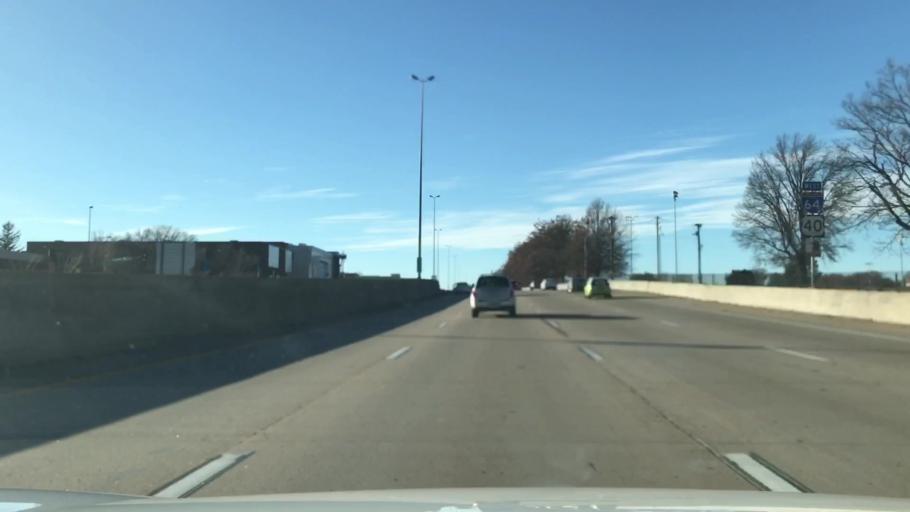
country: US
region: Missouri
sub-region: Saint Louis County
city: University City
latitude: 38.6297
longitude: -90.2731
